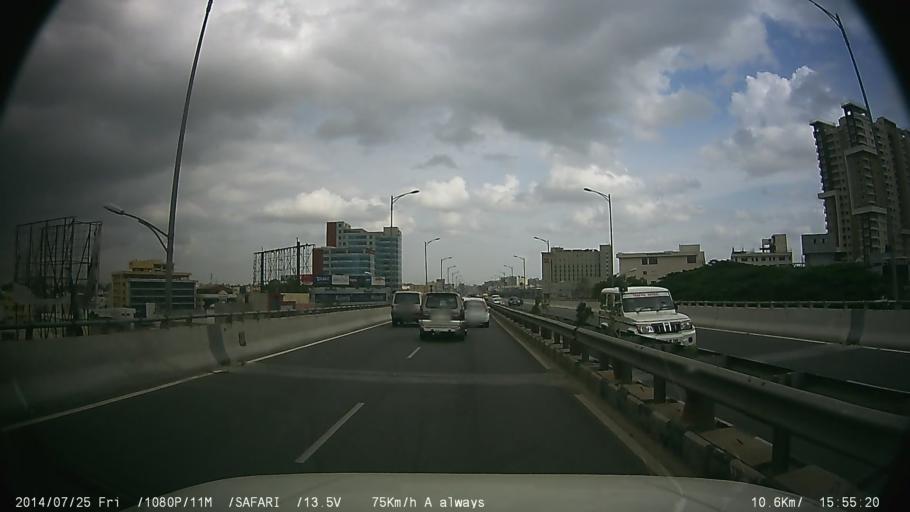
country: IN
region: Karnataka
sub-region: Bangalore Urban
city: Bangalore
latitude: 12.9039
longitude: 77.6310
